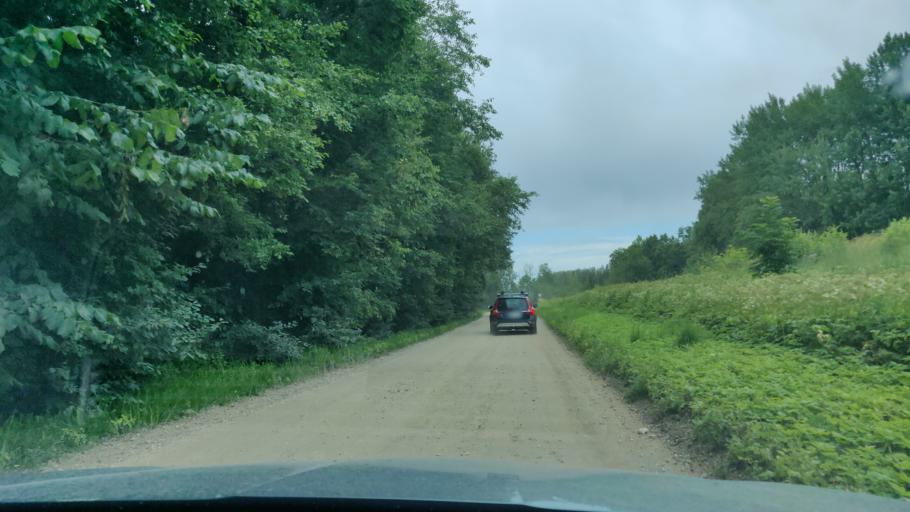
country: EE
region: Vorumaa
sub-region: Antsla vald
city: Vana-Antsla
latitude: 58.0358
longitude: 26.5545
